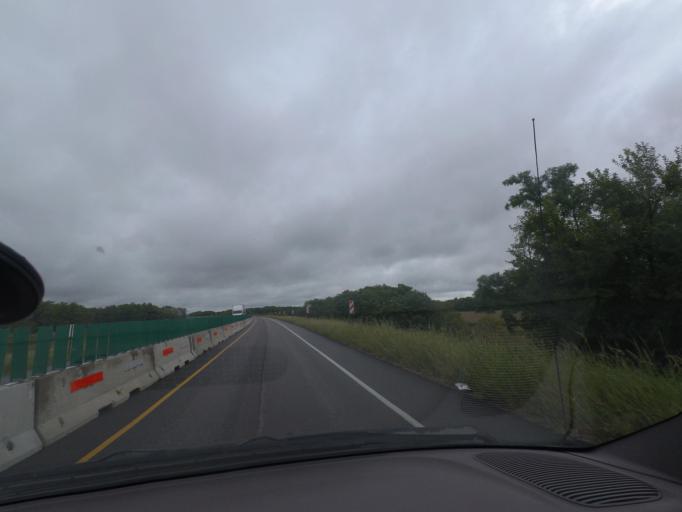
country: US
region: Illinois
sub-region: Piatt County
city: Cerro Gordo
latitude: 39.9802
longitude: -88.7934
